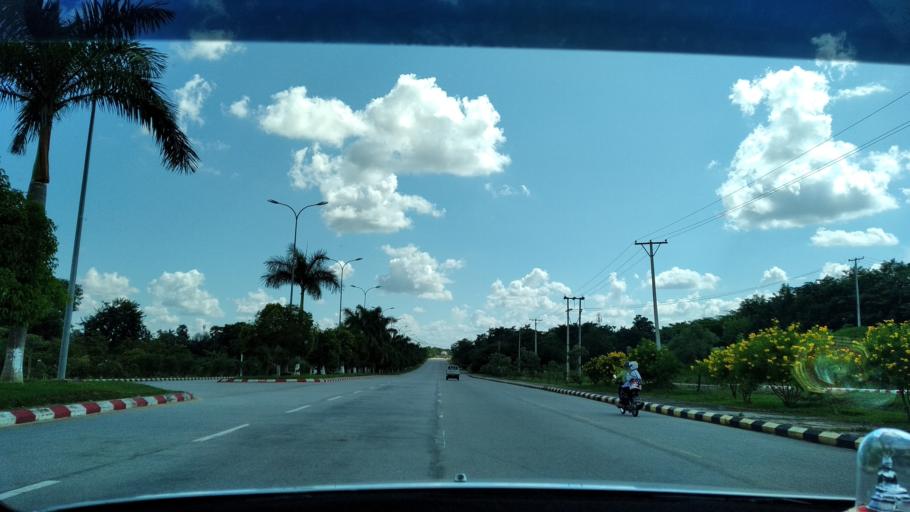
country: MM
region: Mandalay
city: Nay Pyi Taw
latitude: 19.7748
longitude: 96.1429
